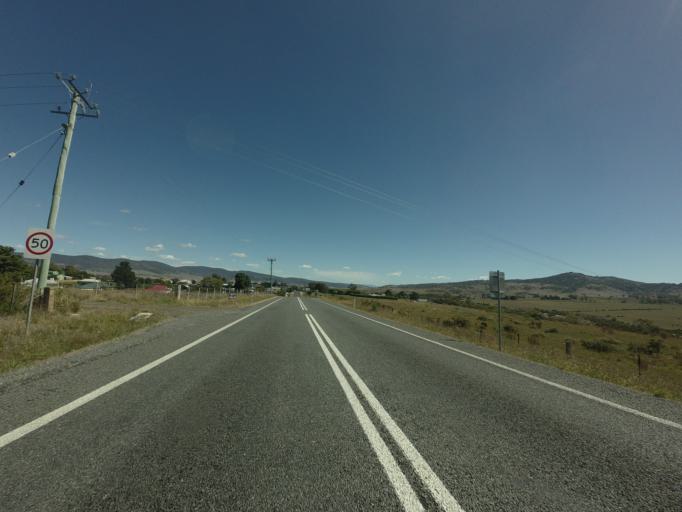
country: AU
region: Tasmania
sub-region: Northern Midlands
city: Evandale
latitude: -41.7790
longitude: 147.7268
